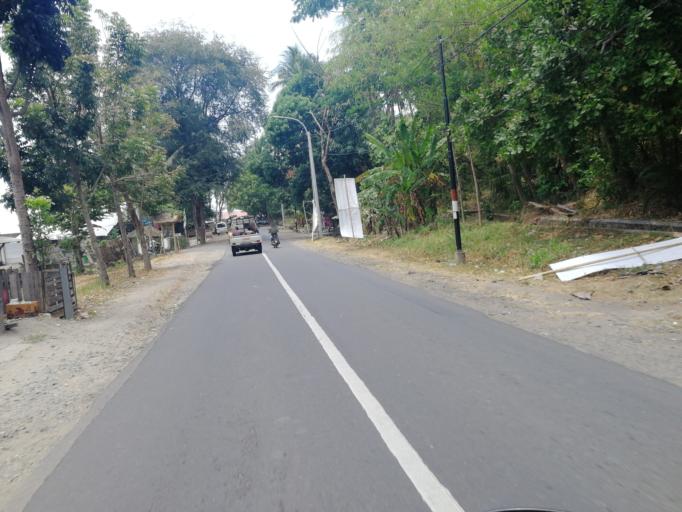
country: ID
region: West Nusa Tenggara
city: Karangsubagan
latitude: -8.4120
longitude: 116.0995
